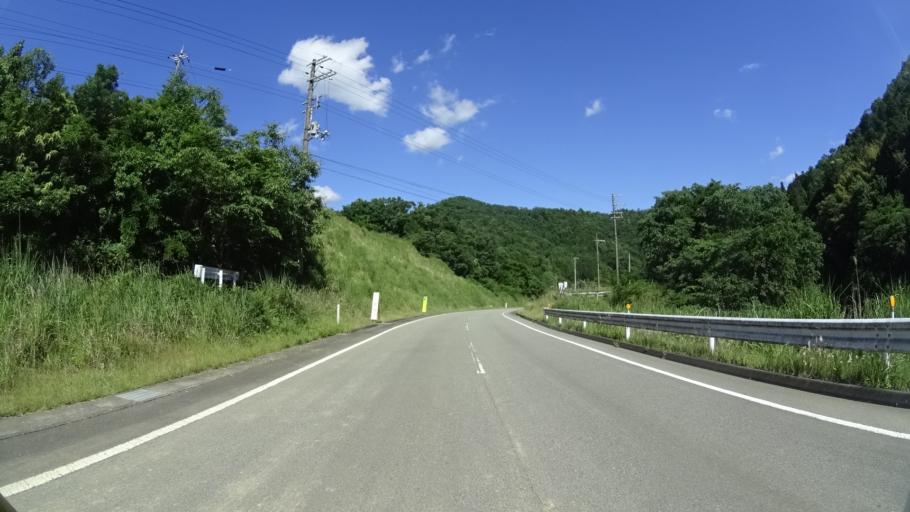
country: JP
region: Kyoto
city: Fukuchiyama
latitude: 35.3719
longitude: 135.0812
